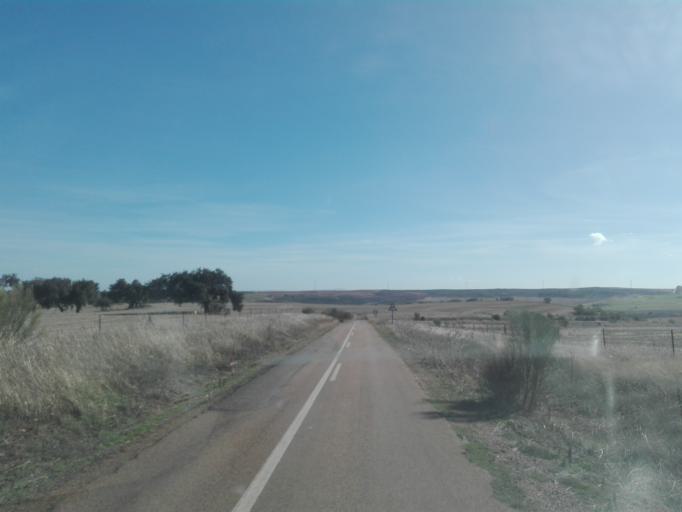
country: ES
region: Extremadura
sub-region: Provincia de Badajoz
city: Maguilla
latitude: 38.3405
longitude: -5.9103
